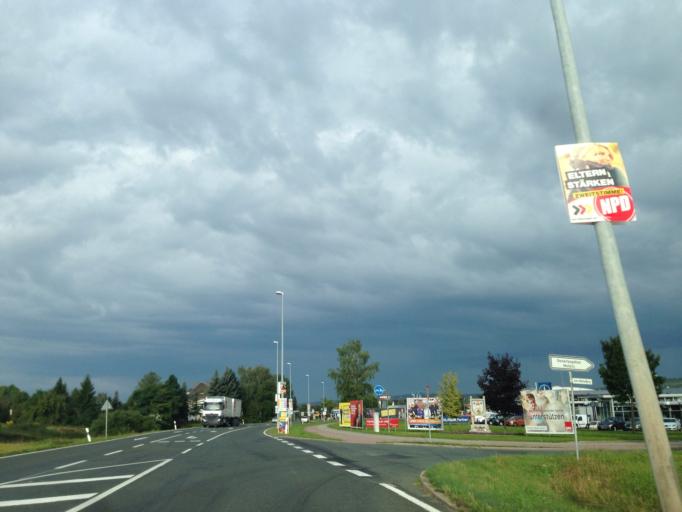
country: DE
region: Thuringia
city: Dreitzsch
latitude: 50.7388
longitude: 11.7741
